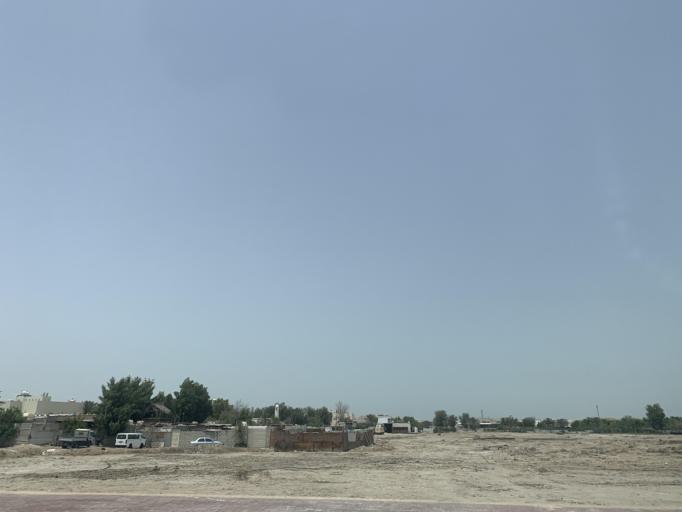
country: BH
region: Northern
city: Sitrah
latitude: 26.1493
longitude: 50.5888
